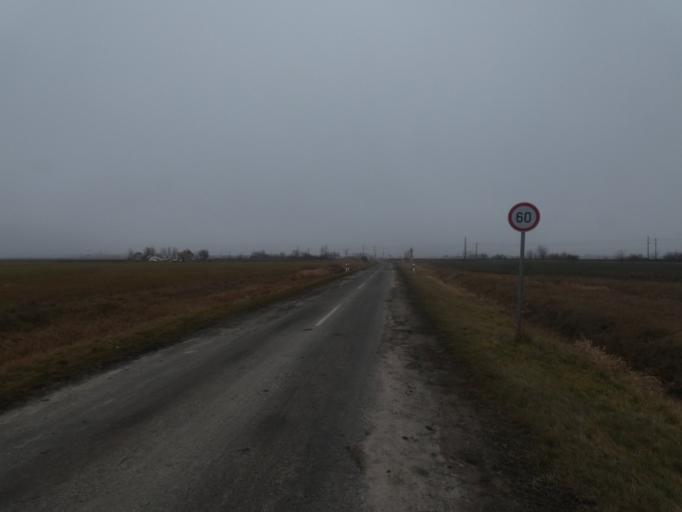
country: HU
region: Pest
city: Tapiogyorgye
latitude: 47.3173
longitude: 19.9697
